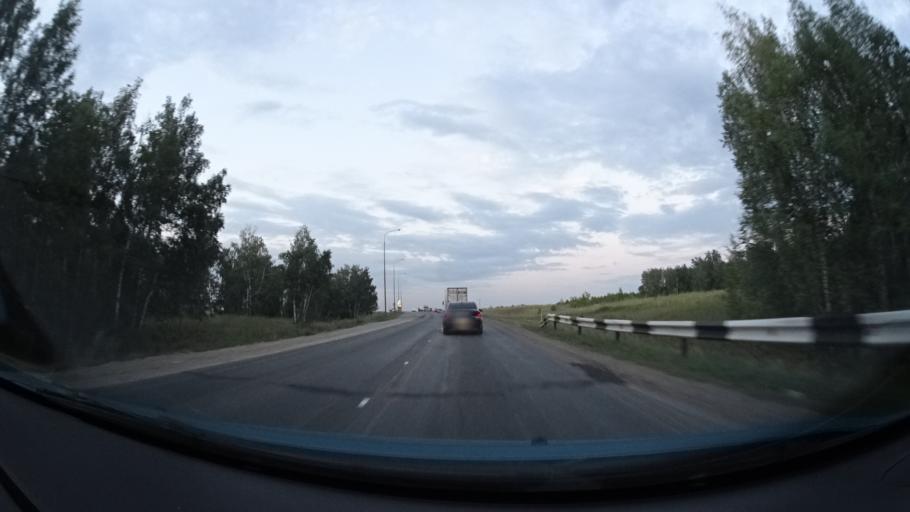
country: RU
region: Tatarstan
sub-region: Bavlinskiy Rayon
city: Bavly
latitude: 54.2691
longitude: 52.9699
